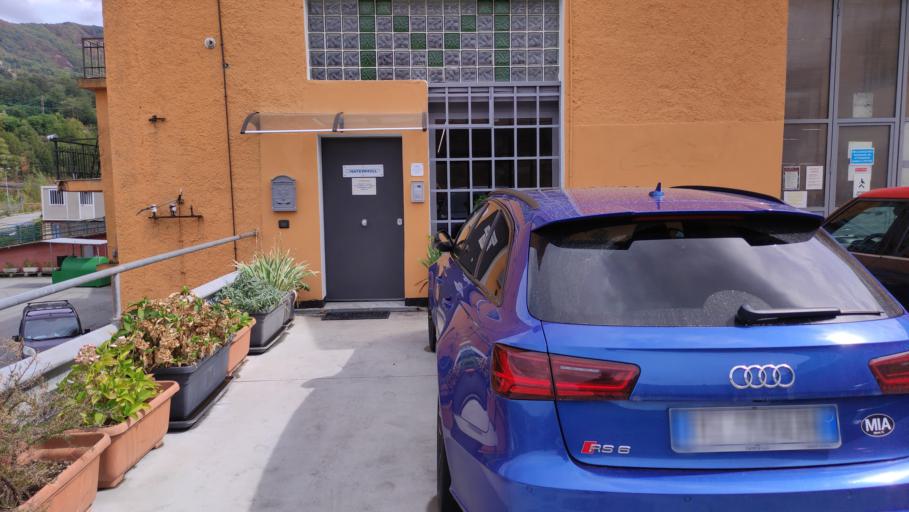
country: IT
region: Liguria
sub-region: Provincia di Genova
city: Busalla
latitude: 44.5680
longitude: 8.9613
